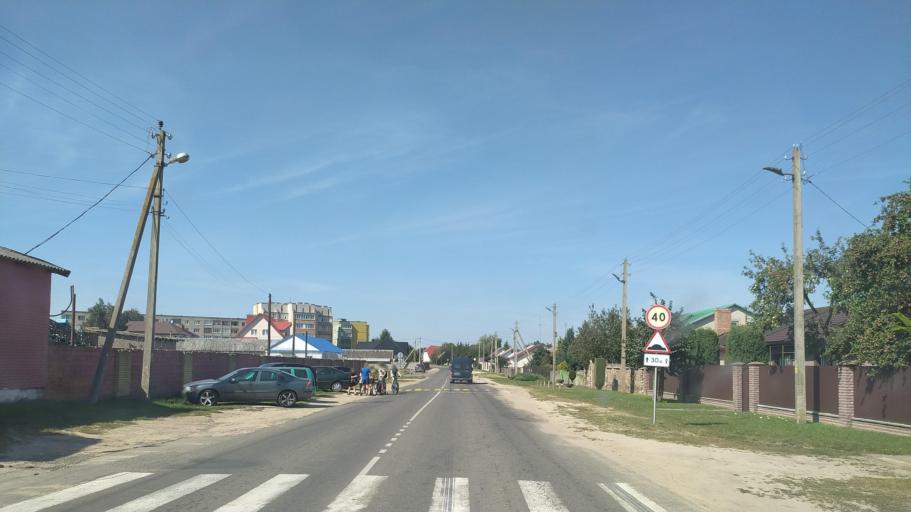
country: BY
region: Brest
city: Byaroza
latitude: 52.5263
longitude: 24.9889
